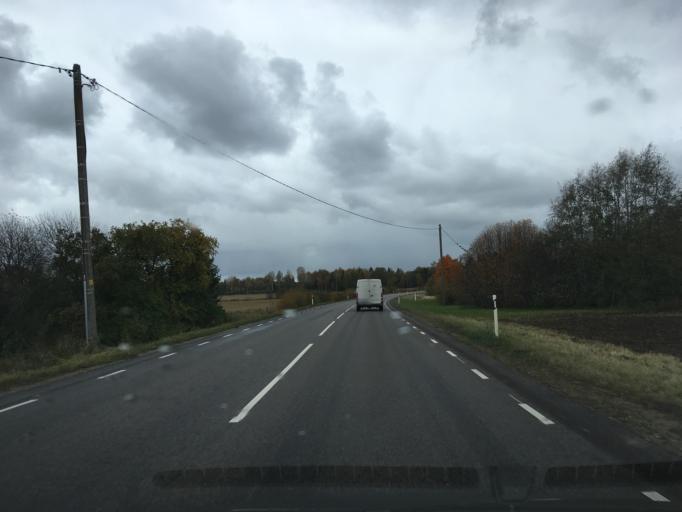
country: EE
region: Harju
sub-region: Anija vald
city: Kehra
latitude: 59.3303
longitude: 25.3180
